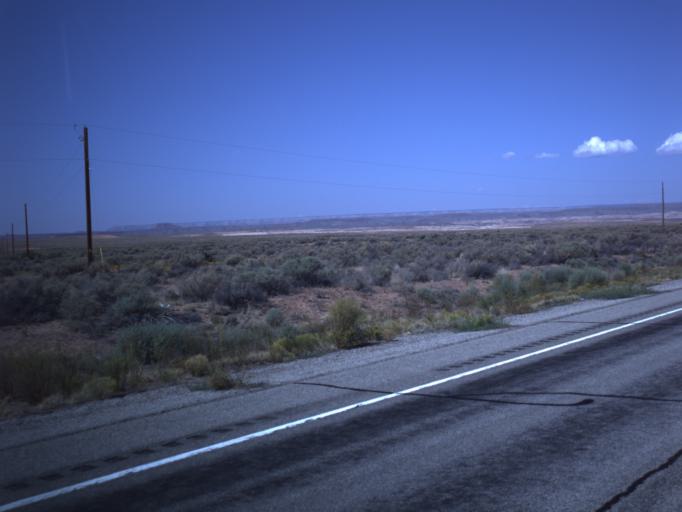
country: US
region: Utah
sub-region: San Juan County
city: Blanding
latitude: 37.1861
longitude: -109.5923
